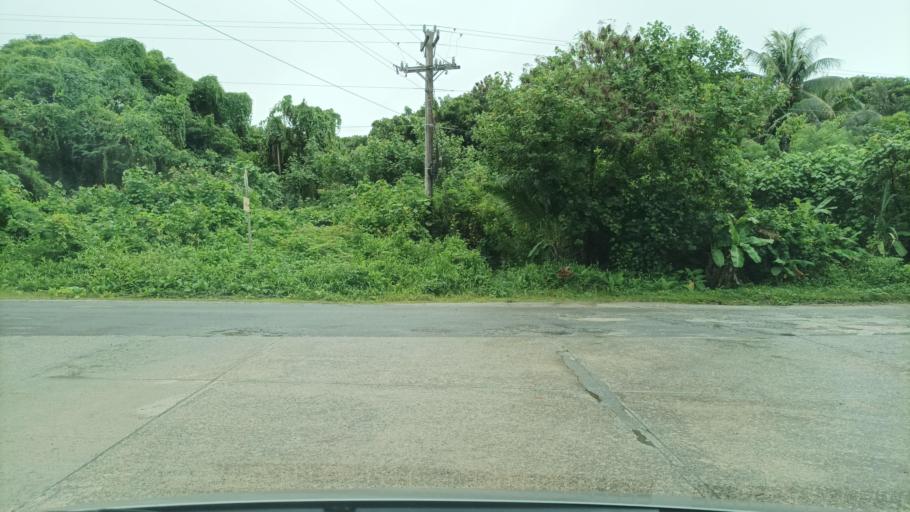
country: FM
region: Yap
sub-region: Weloy Municipality
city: Colonia
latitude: 9.5475
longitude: 138.1549
